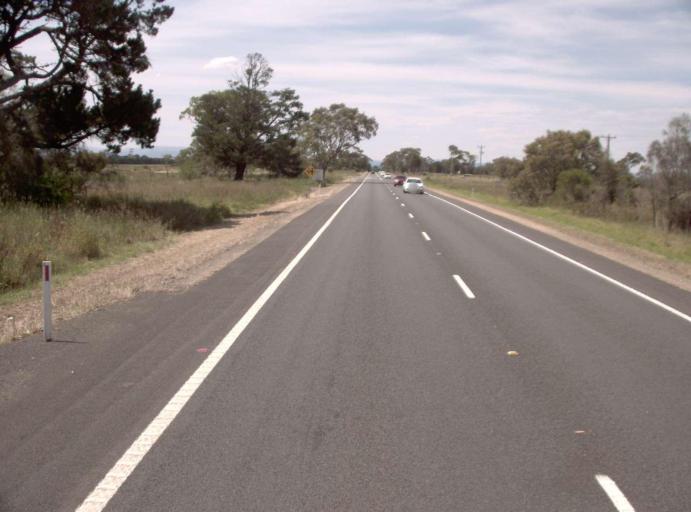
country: AU
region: Victoria
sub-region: Wellington
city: Sale
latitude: -38.0057
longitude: 147.0630
